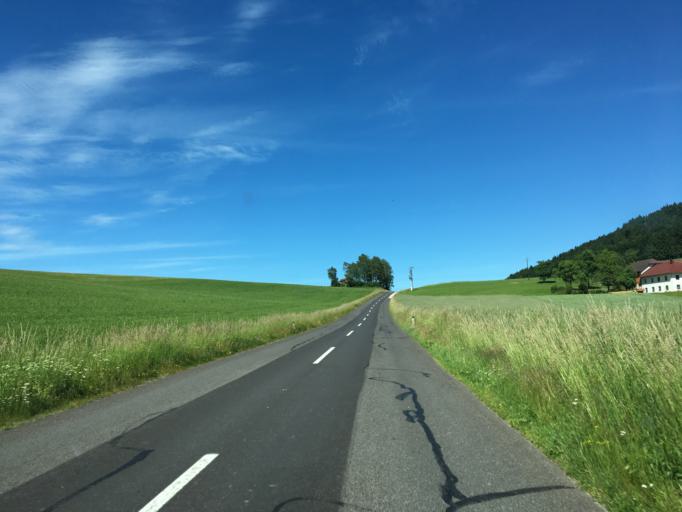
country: AT
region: Upper Austria
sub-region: Politischer Bezirk Urfahr-Umgebung
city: Eidenberg
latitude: 48.4126
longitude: 14.2186
